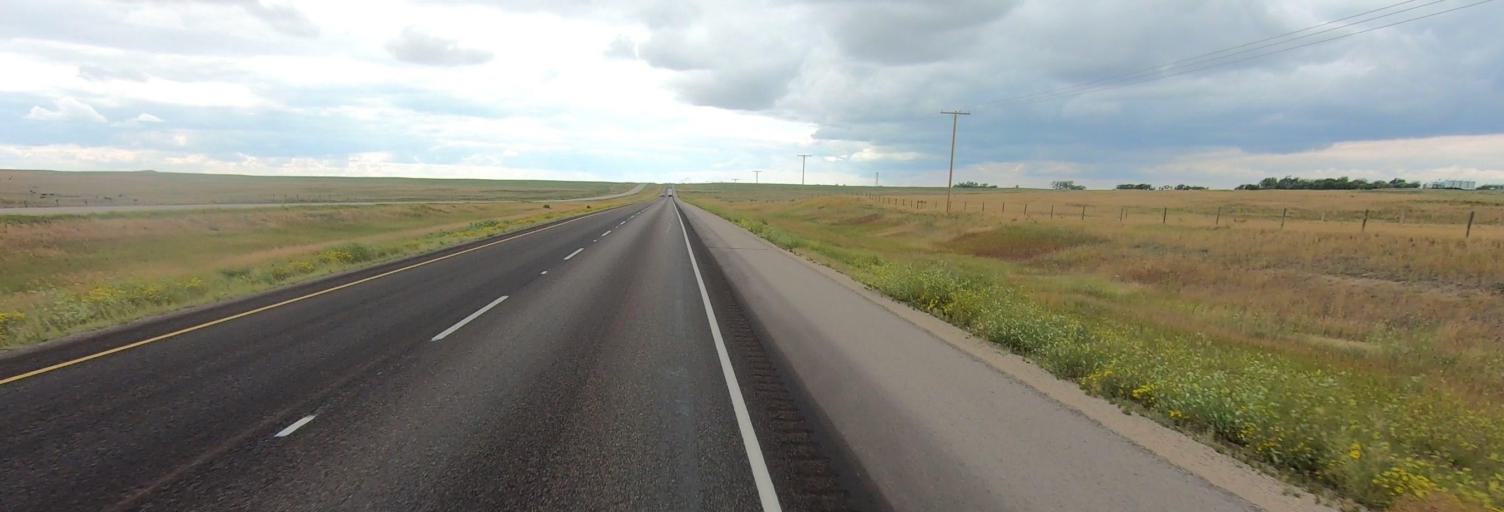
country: CA
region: Saskatchewan
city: Shaunavon
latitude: 50.0706
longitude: -108.6983
